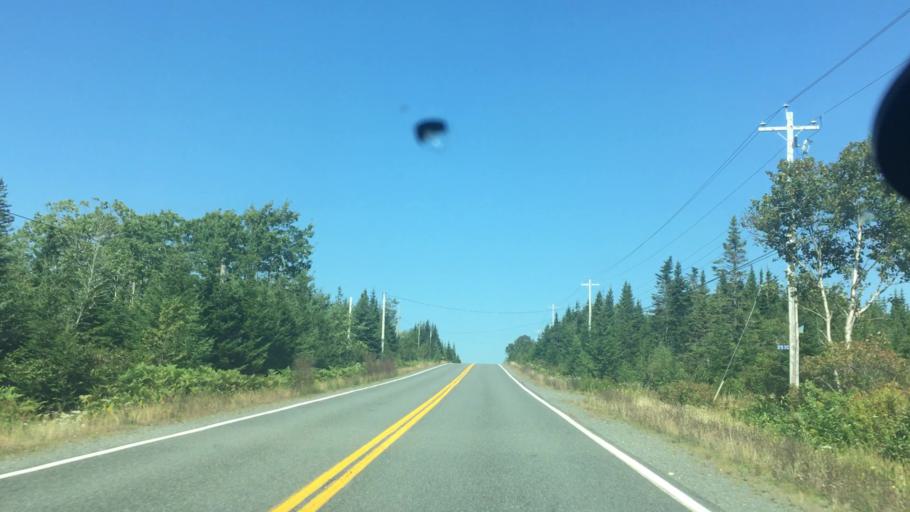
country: CA
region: Nova Scotia
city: Antigonish
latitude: 45.0027
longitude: -62.1014
